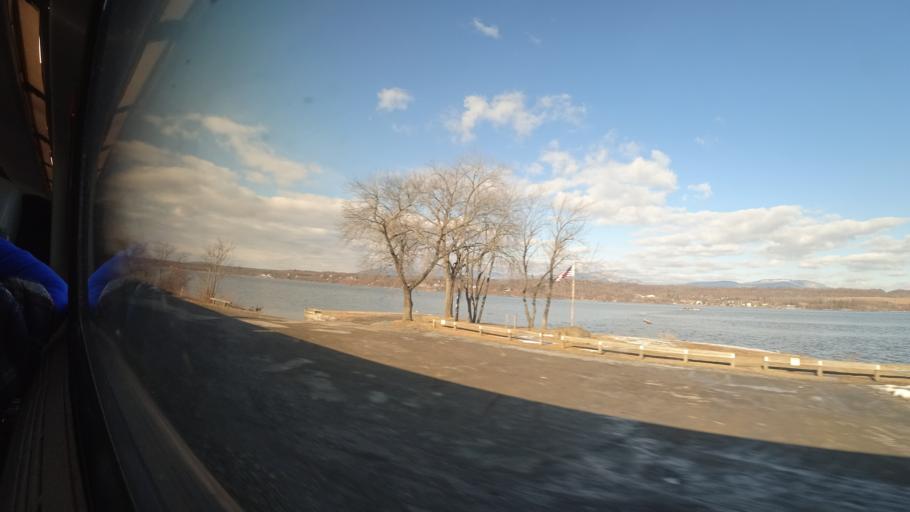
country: US
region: New York
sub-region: Dutchess County
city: Tivoli
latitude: 42.1260
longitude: -73.9042
